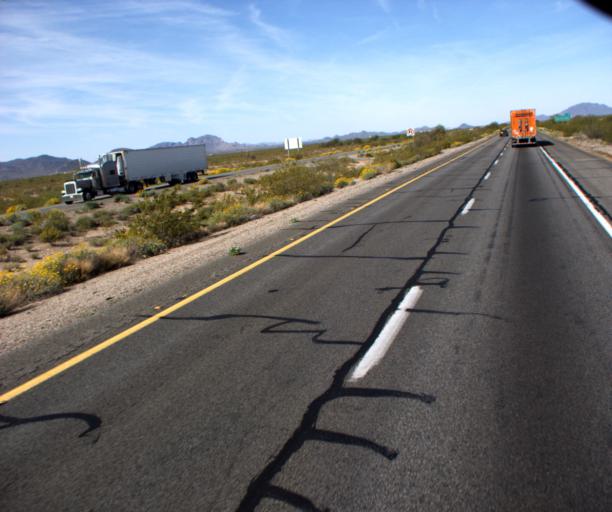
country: US
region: Arizona
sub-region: Maricopa County
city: Buckeye
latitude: 33.4779
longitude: -112.8489
